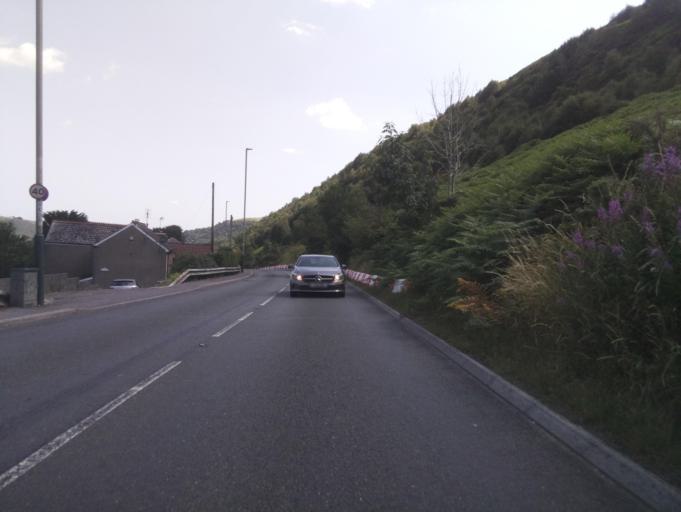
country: GB
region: Wales
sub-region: Caerphilly County Borough
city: New Tredegar
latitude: 51.7269
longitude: -3.2559
